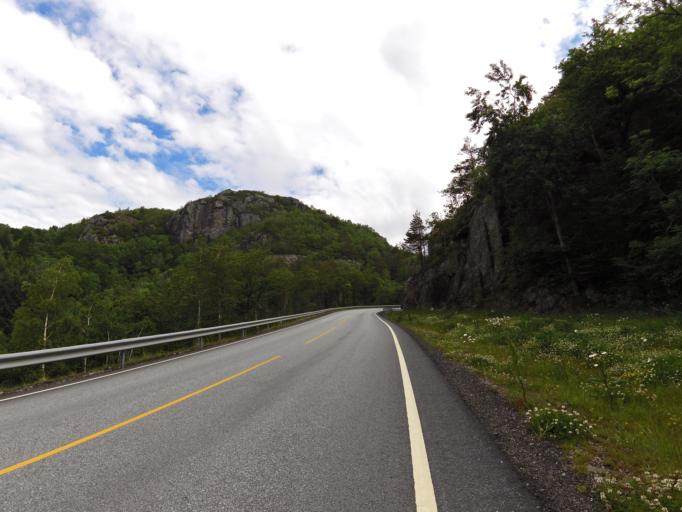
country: NO
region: Vest-Agder
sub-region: Lindesnes
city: Vigeland
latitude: 58.0516
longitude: 7.2065
